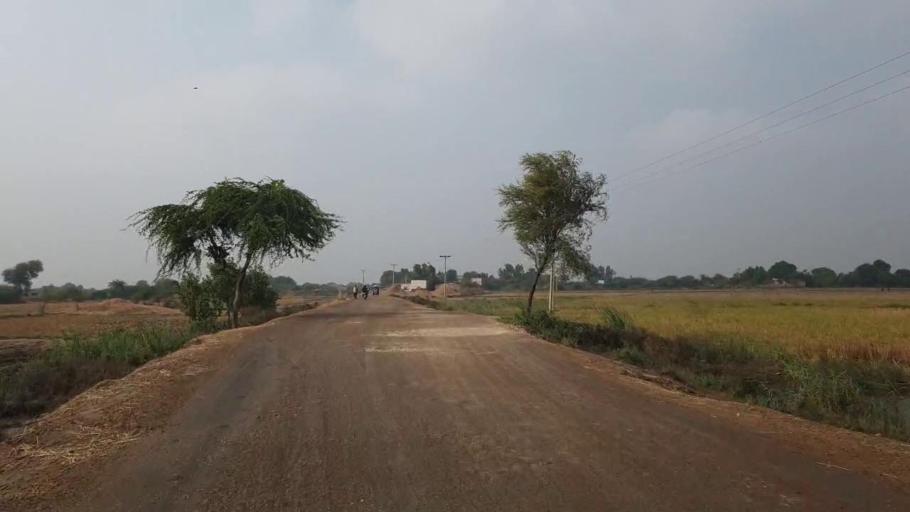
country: PK
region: Sindh
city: Matli
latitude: 24.9713
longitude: 68.6033
